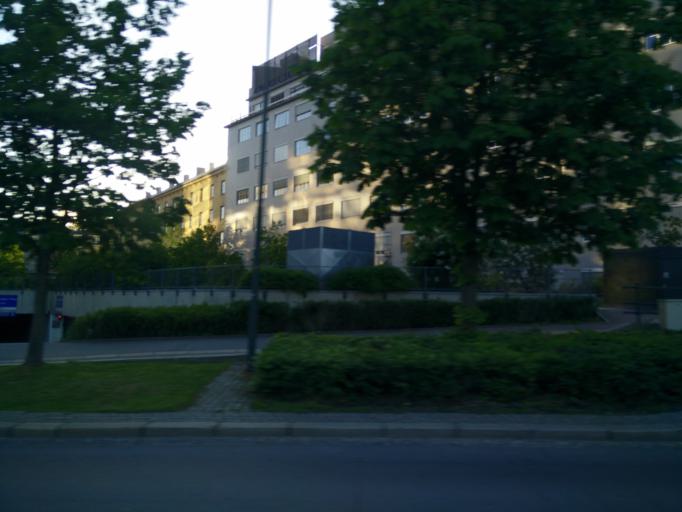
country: NO
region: Oslo
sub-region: Oslo
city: Oslo
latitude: 59.9116
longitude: 10.7256
